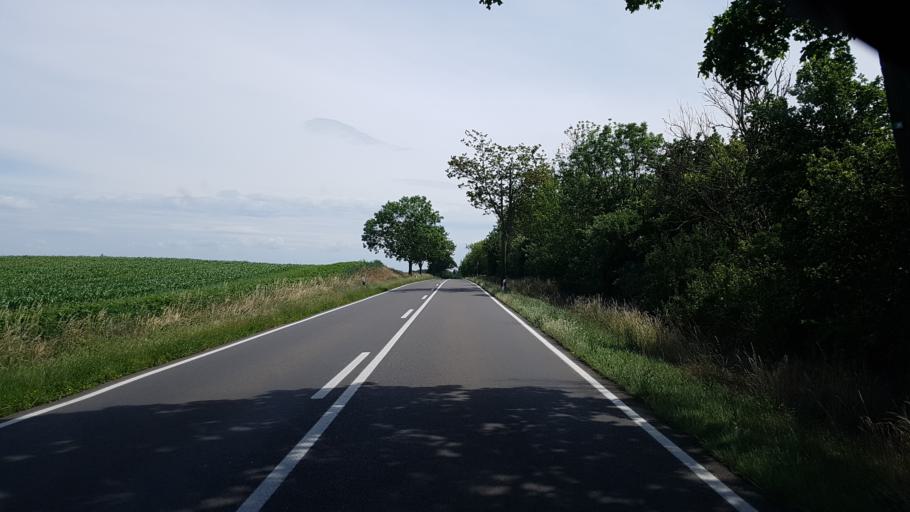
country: DE
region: Brandenburg
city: Prenzlau
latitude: 53.3707
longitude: 13.7886
